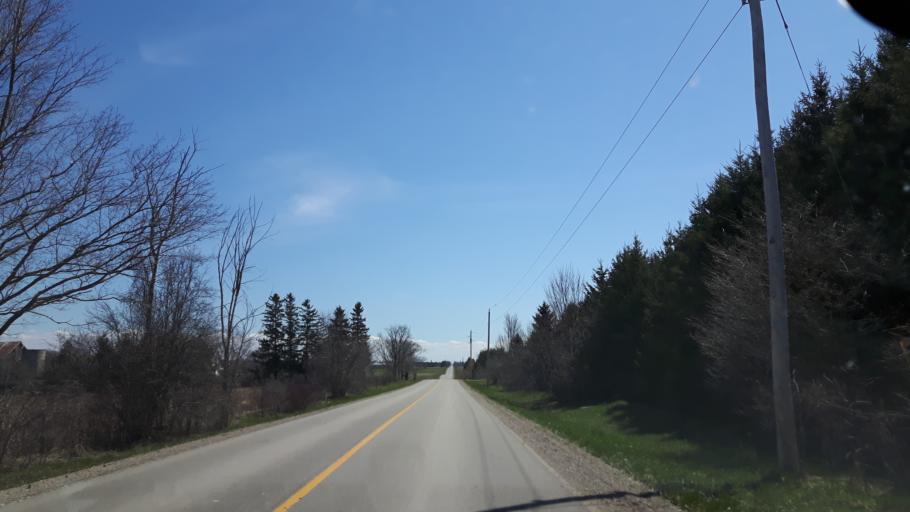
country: CA
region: Ontario
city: Goderich
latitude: 43.6537
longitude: -81.6441
